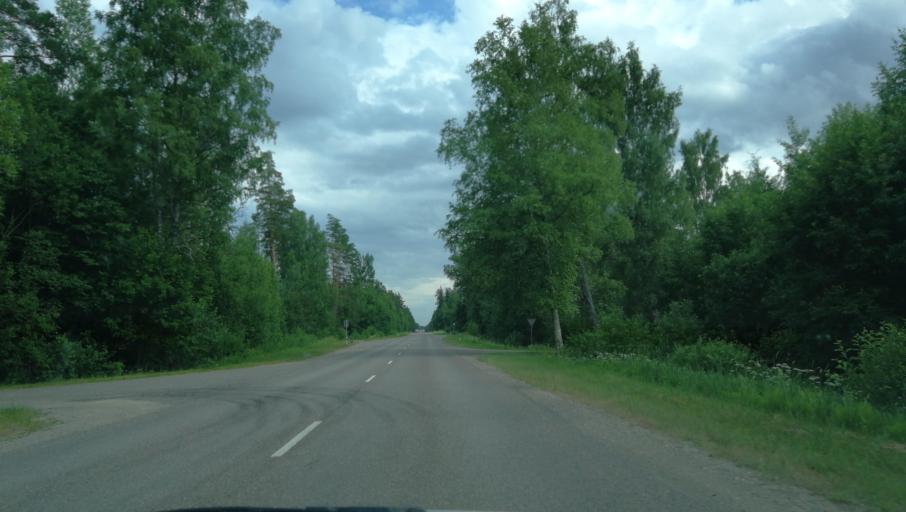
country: LV
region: Naukseni
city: Naukseni
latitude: 57.8154
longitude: 25.4028
